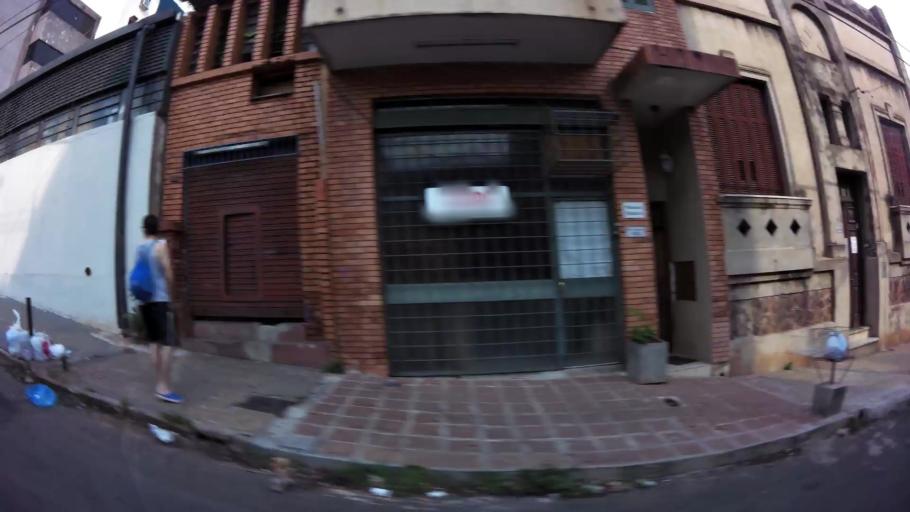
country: PY
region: Asuncion
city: Asuncion
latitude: -25.2960
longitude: -57.6258
